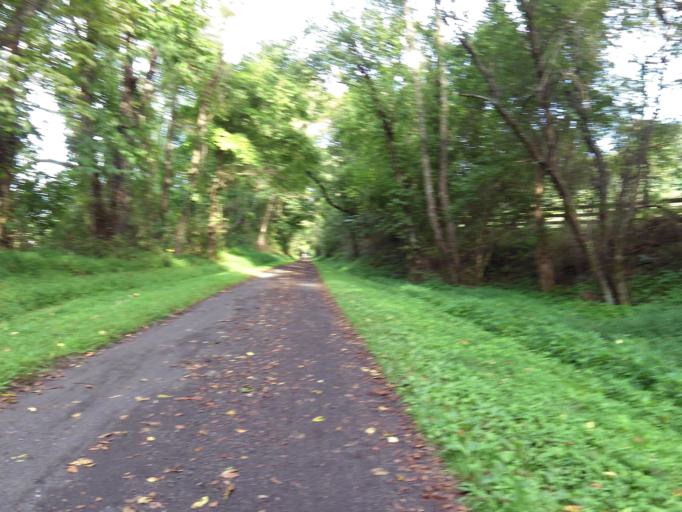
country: US
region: Virginia
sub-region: Washington County
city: Abingdon
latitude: 36.6974
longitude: -81.9494
